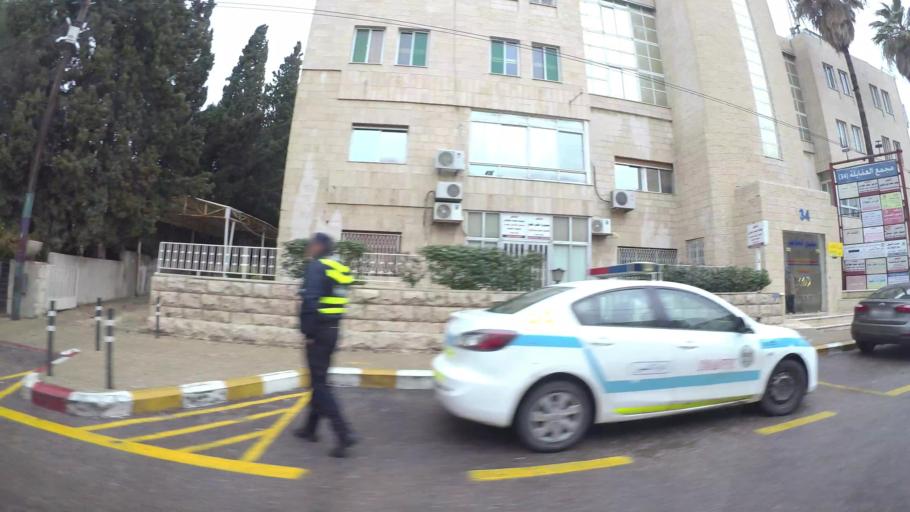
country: JO
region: Amman
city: Amman
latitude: 31.9503
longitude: 35.9045
